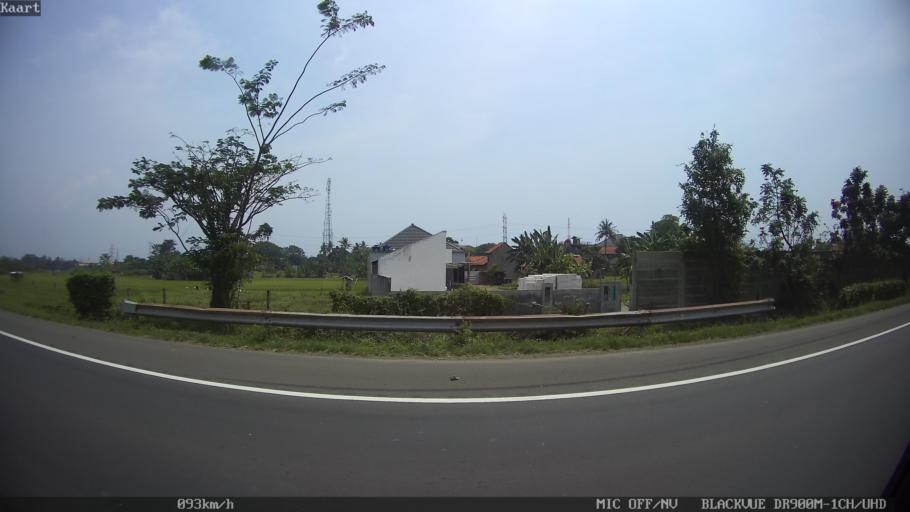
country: ID
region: Banten
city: Curug
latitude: -5.9768
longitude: 106.0110
